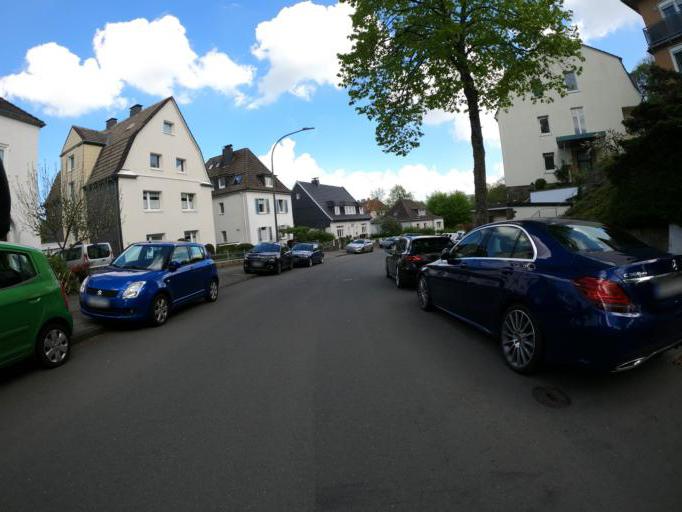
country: DE
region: North Rhine-Westphalia
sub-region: Regierungsbezirk Dusseldorf
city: Wuppertal
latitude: 51.2485
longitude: 7.1570
